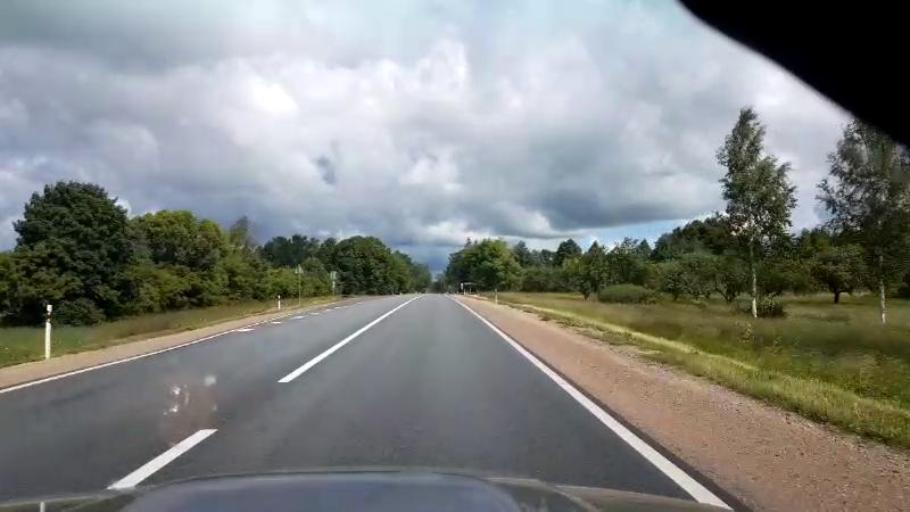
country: LV
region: Lecava
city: Iecava
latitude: 56.5261
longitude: 24.1711
